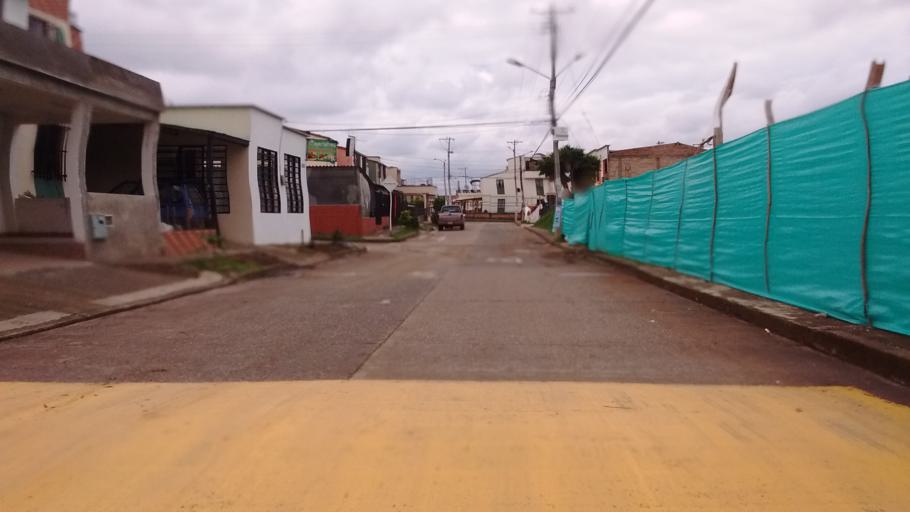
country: CO
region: Cauca
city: Popayan
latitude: 2.4807
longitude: -76.5783
